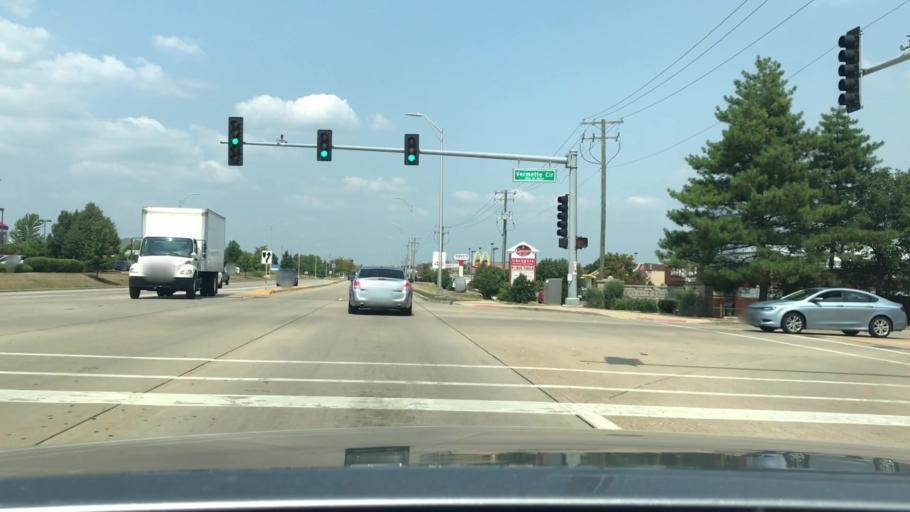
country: US
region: Illinois
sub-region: Will County
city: Shorewood
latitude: 41.5607
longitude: -88.2001
